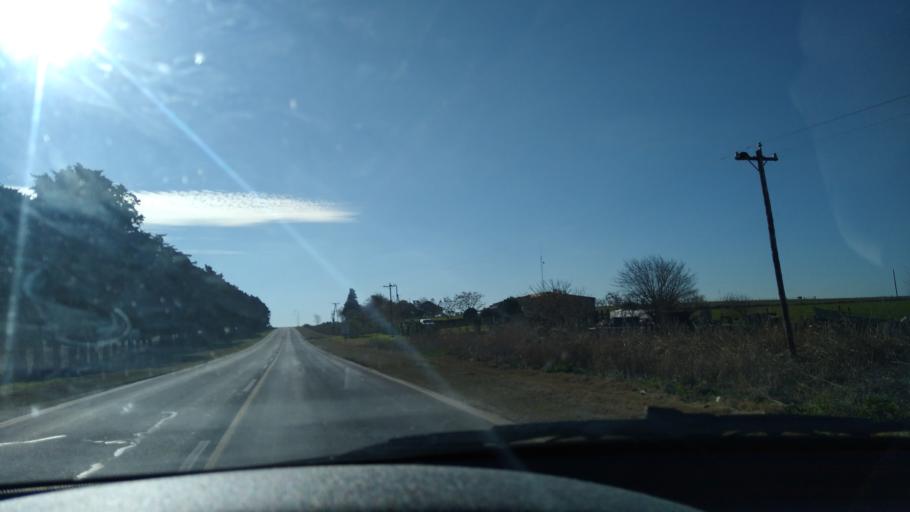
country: AR
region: Entre Rios
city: Aranguren
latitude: -32.4179
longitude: -60.3170
